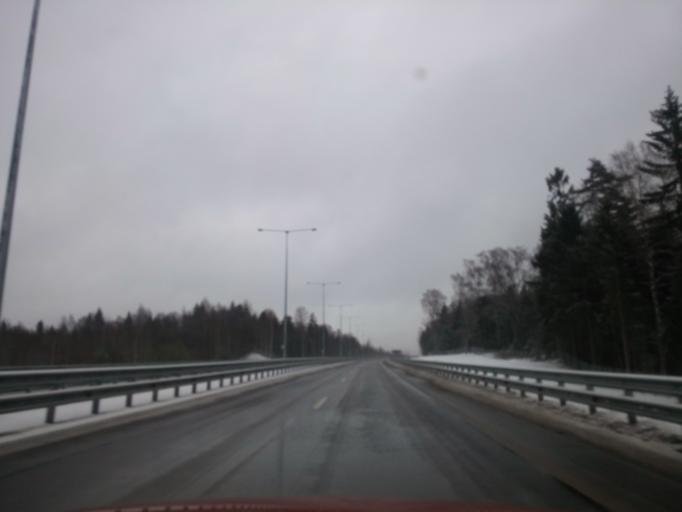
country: RU
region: Tverskaya
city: Likhoslavl'
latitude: 56.9700
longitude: 35.4603
